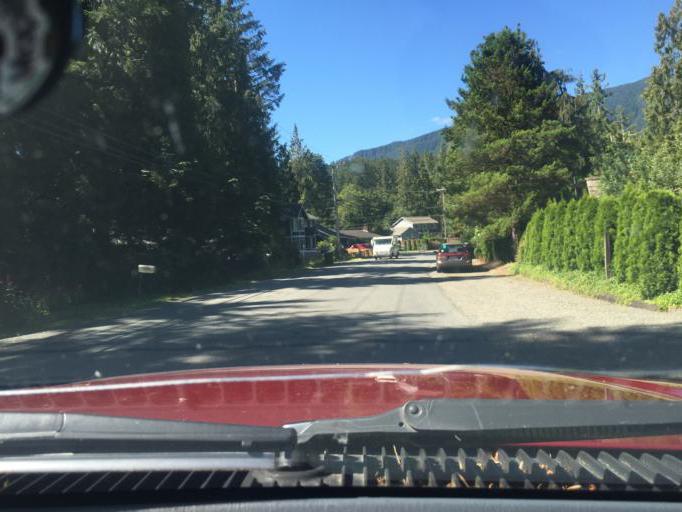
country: US
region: Washington
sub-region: King County
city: Riverbend
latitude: 47.4667
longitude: -121.7511
